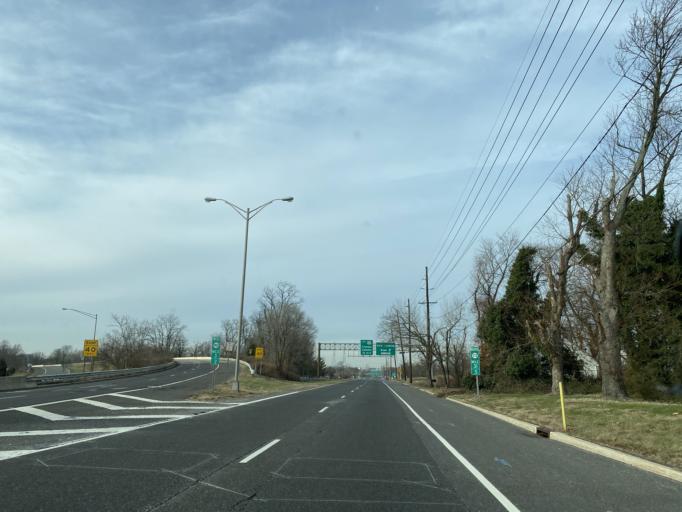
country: US
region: New Jersey
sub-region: Burlington County
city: Cinnaminson
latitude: 39.9746
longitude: -75.0098
